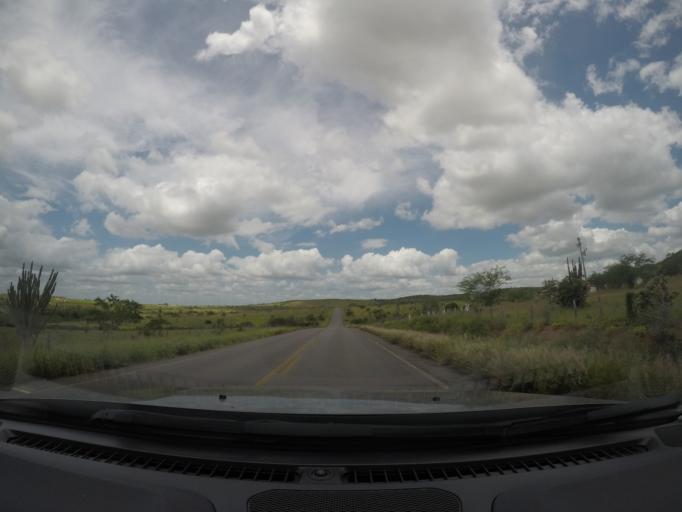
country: BR
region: Bahia
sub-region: Ipira
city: Ipira
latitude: -12.2607
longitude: -39.8275
